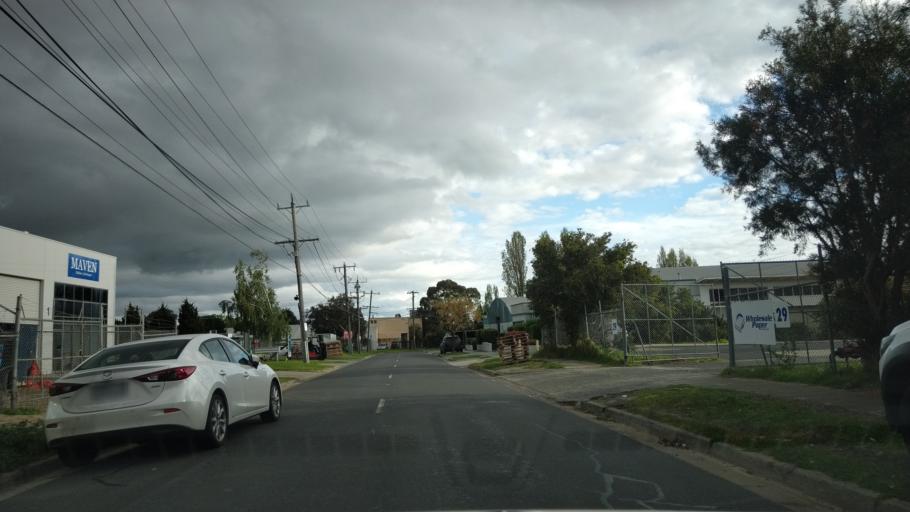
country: AU
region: Victoria
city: Highett
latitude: -37.9501
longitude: 145.0665
